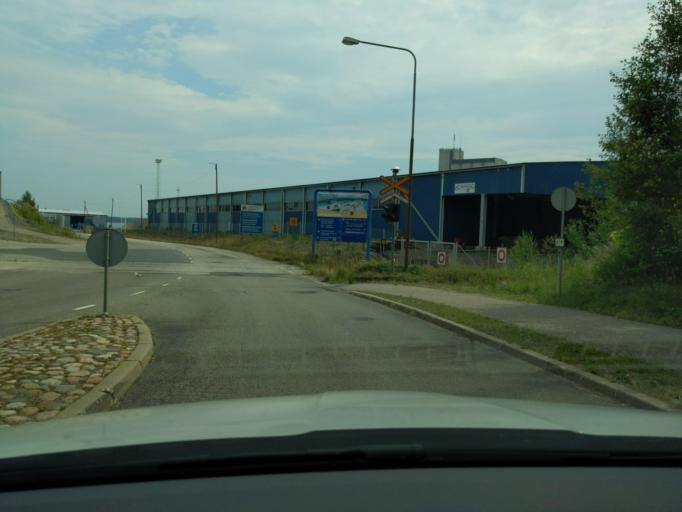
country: FI
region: Uusimaa
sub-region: Loviisa
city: Lovisa
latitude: 60.4115
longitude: 26.2487
